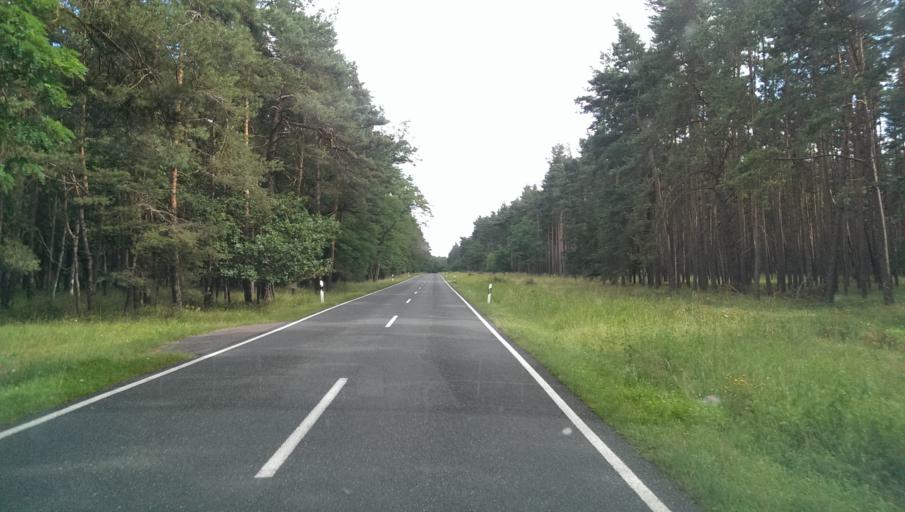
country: DE
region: Saxony-Anhalt
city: Radis
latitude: 51.7760
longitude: 12.4907
